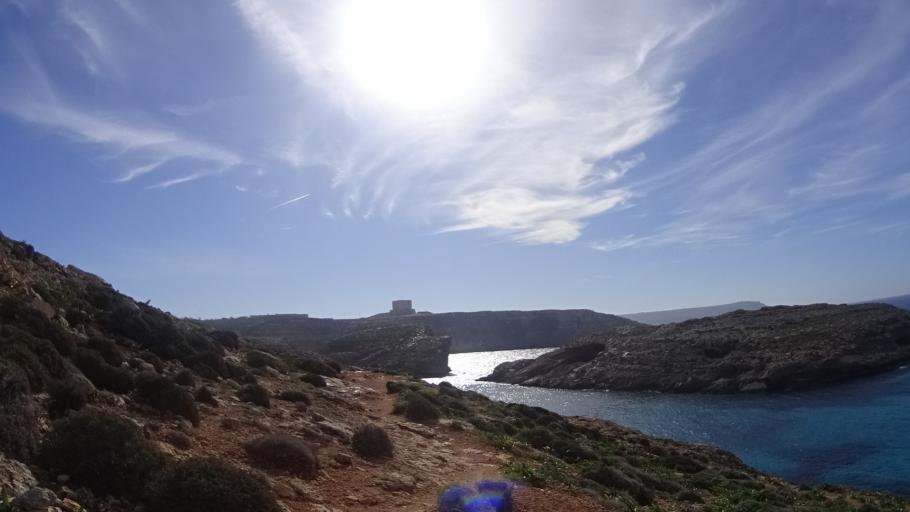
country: MT
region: Il-Qala
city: Qala
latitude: 36.0125
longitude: 14.3250
